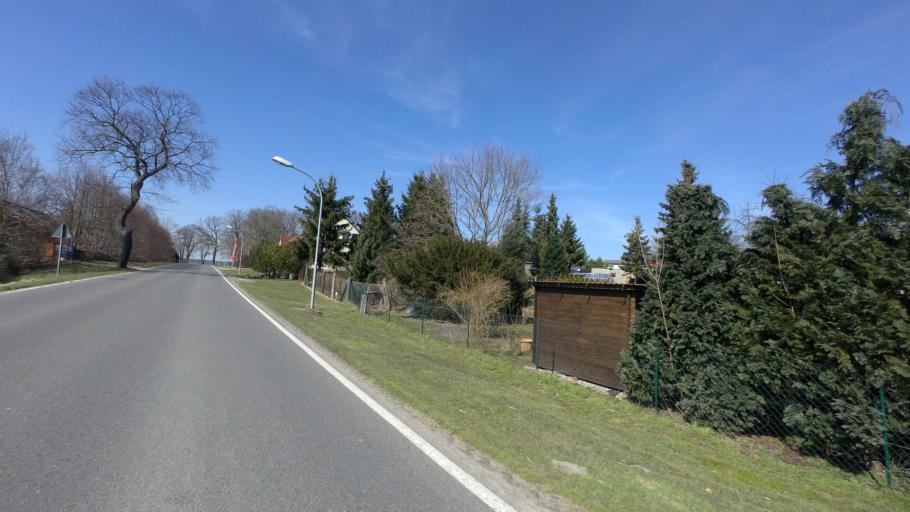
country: DE
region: Brandenburg
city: Protzel
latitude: 52.6309
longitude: 14.0125
